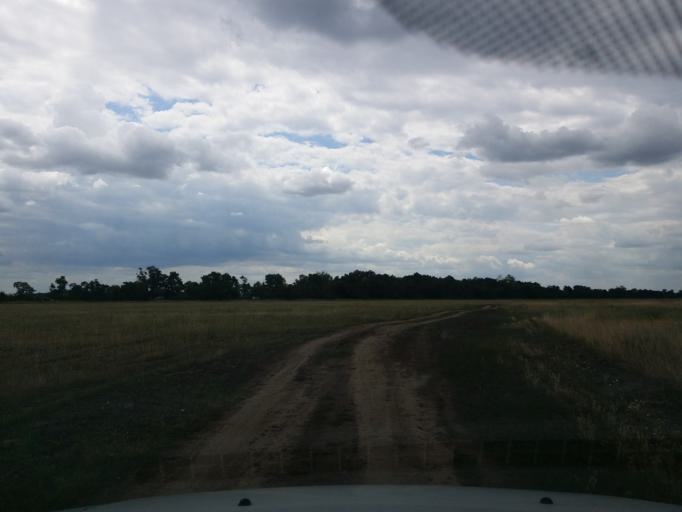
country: HU
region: Hajdu-Bihar
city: Egyek
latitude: 47.5522
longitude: 20.9416
